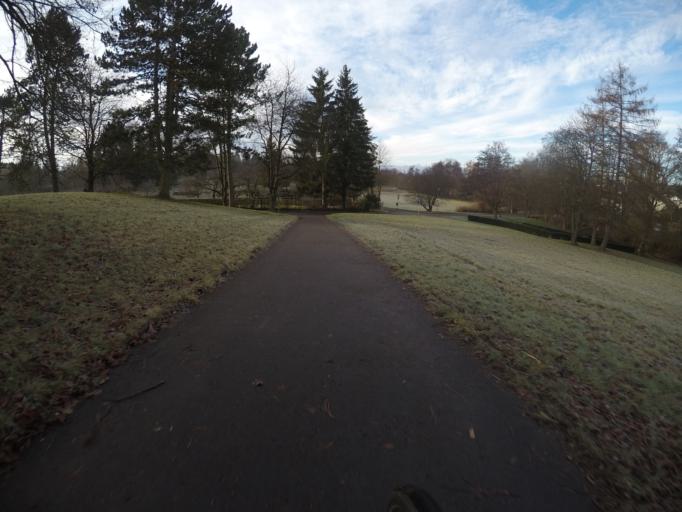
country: DE
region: Baden-Wuerttemberg
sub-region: Regierungsbezirk Stuttgart
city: Sindelfingen
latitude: 48.7179
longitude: 9.0121
